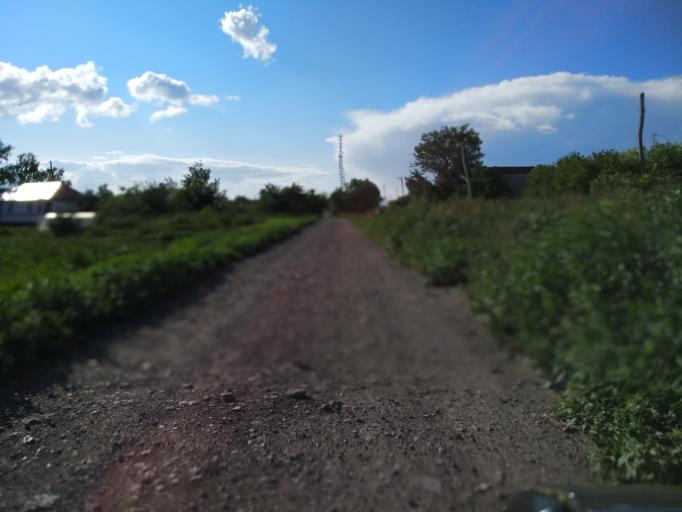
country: RU
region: Lipetsk
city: Dobrinka
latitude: 52.0334
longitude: 40.5620
